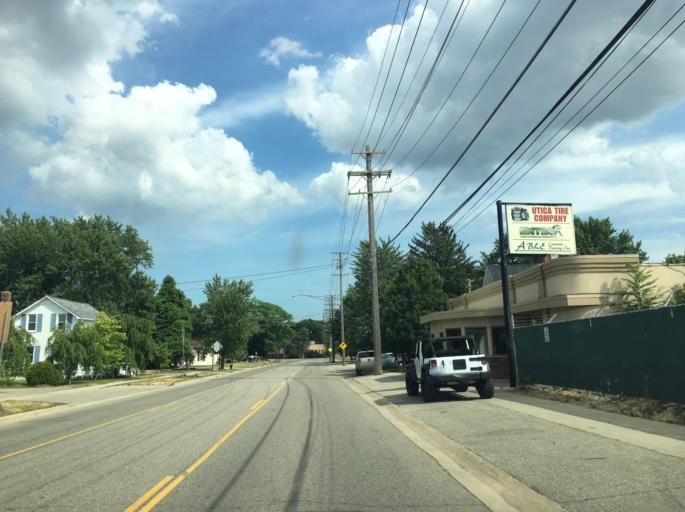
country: US
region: Michigan
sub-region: Macomb County
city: Utica
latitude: 42.6239
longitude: -83.0405
